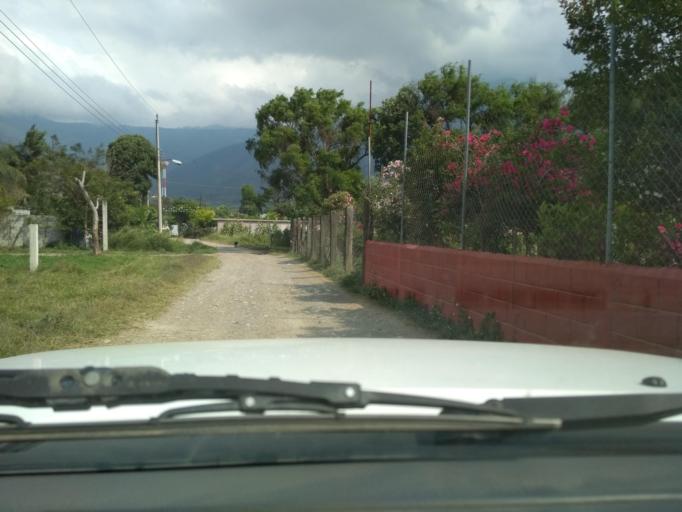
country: MX
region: Veracruz
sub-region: Acultzingo
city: Sierra de Agua
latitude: 18.7626
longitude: -97.2309
